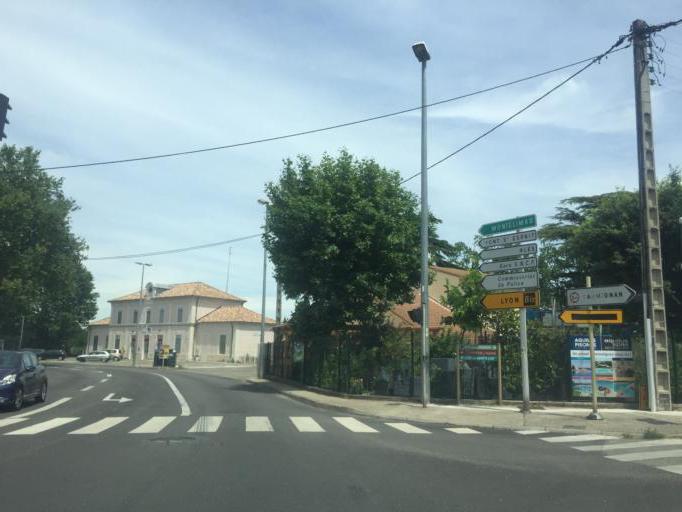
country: FR
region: Languedoc-Roussillon
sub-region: Departement du Gard
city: Bagnols-sur-Ceze
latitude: 44.1609
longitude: 4.6263
